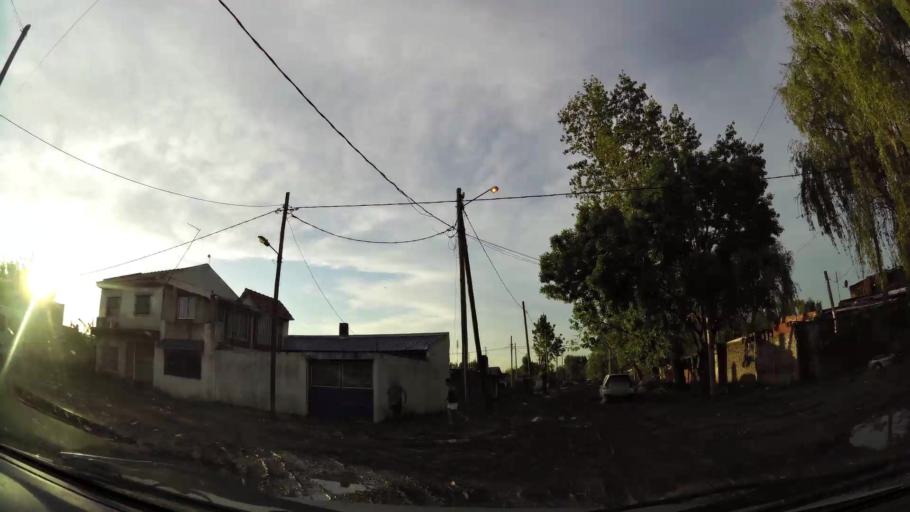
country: AR
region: Buenos Aires
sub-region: Partido de Almirante Brown
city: Adrogue
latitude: -34.7702
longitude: -58.3424
